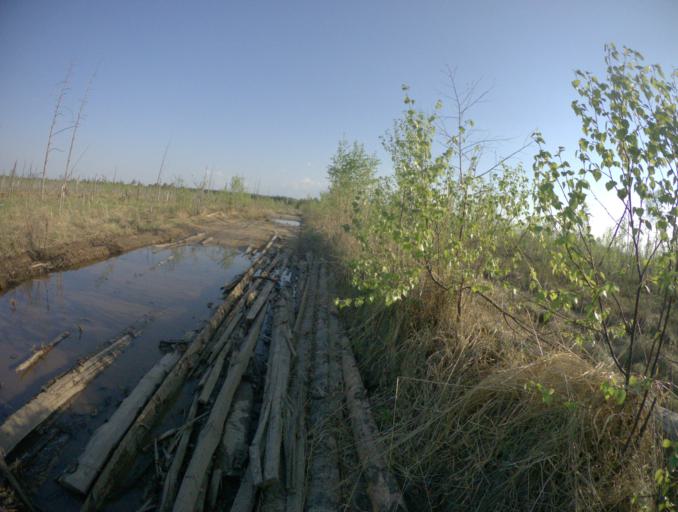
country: RU
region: Vladimir
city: Vyazniki
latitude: 56.3847
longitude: 42.1726
